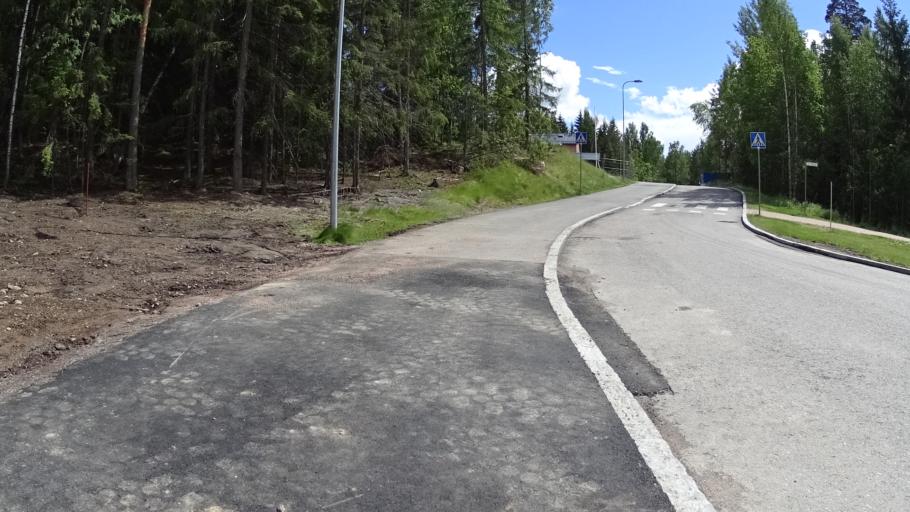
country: FI
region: Uusimaa
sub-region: Helsinki
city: Kauniainen
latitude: 60.2328
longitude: 24.6928
